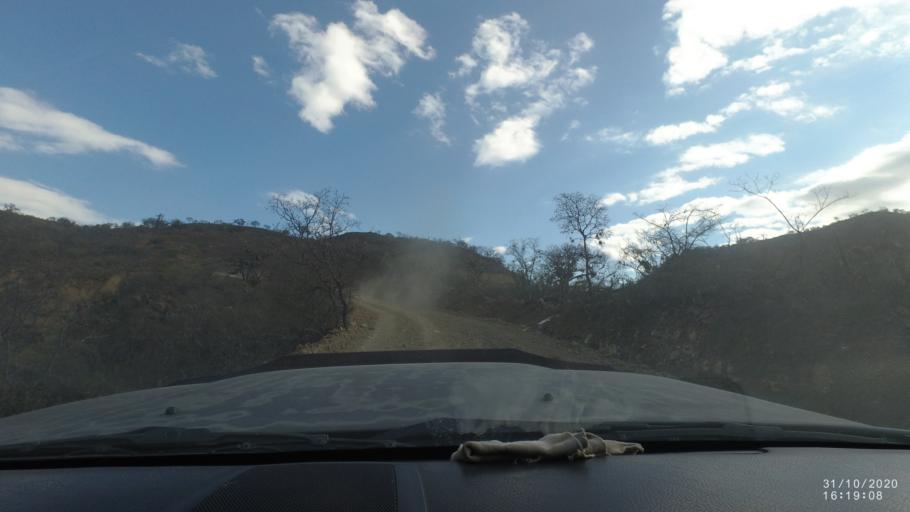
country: BO
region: Chuquisaca
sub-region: Provincia Zudanez
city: Mojocoya
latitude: -18.3945
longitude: -64.6029
